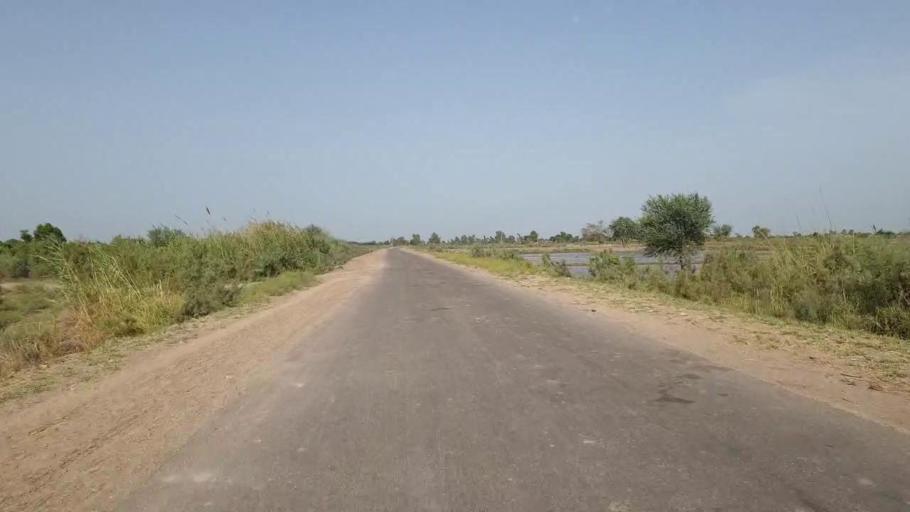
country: PK
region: Sindh
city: Sakrand
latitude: 26.2845
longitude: 68.2438
